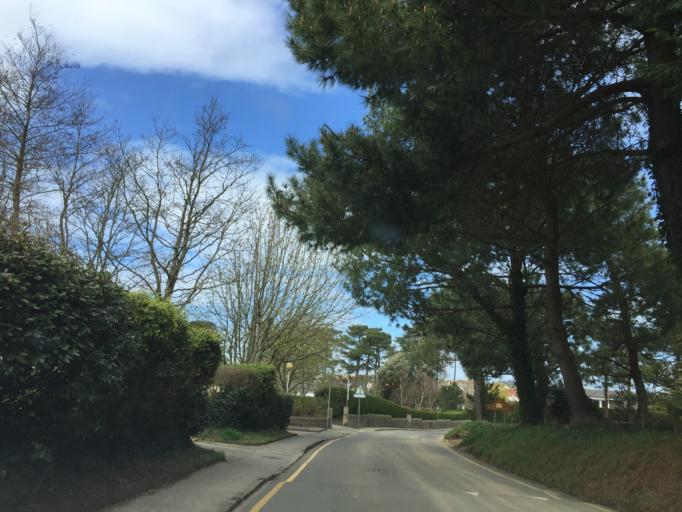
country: JE
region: St Helier
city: Saint Helier
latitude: 49.1927
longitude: -2.1963
